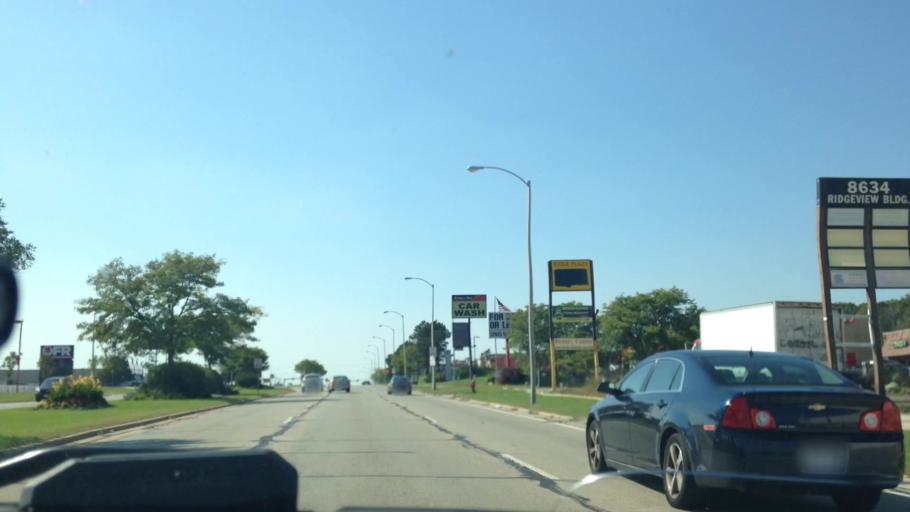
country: US
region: Wisconsin
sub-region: Milwaukee County
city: Brown Deer
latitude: 43.1778
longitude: -88.0187
